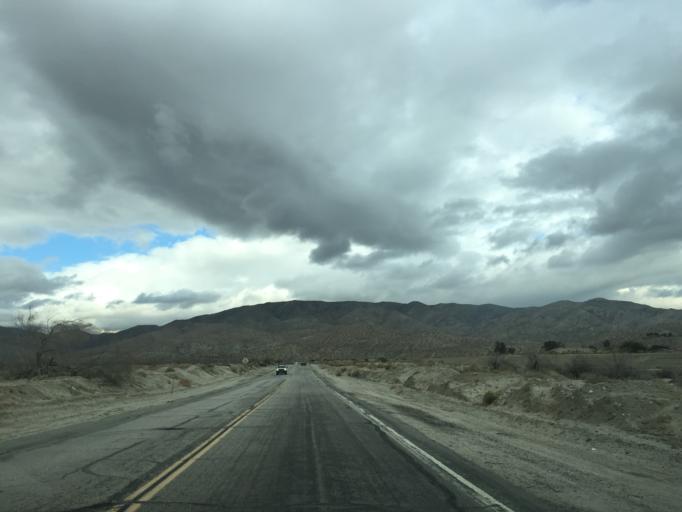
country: US
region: California
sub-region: Riverside County
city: Desert Hot Springs
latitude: 33.9775
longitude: -116.5449
